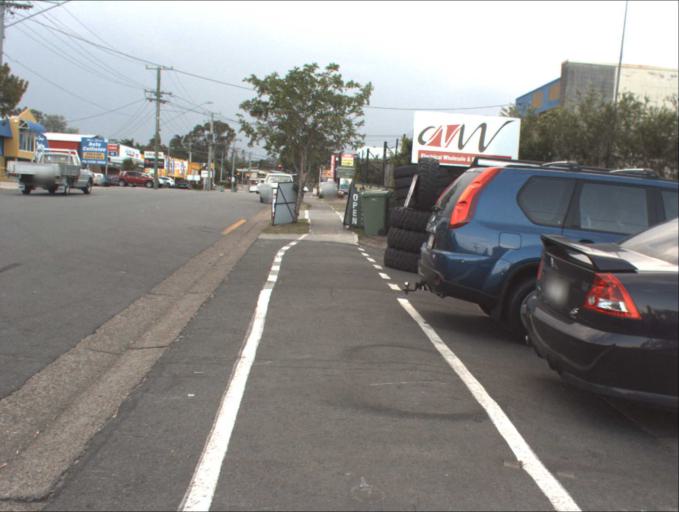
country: AU
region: Queensland
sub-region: Logan
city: Springwood
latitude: -27.6242
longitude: 153.1189
